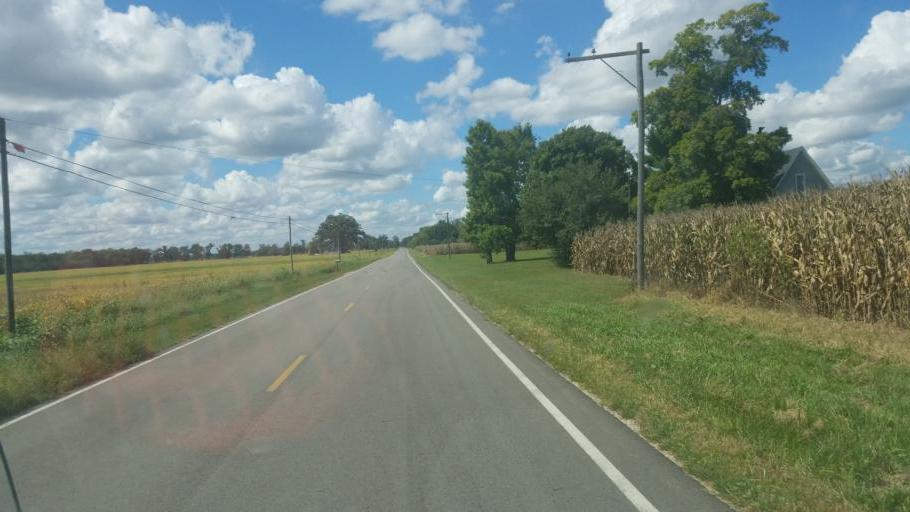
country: US
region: Ohio
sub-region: Champaign County
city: North Lewisburg
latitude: 40.1880
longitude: -83.4613
